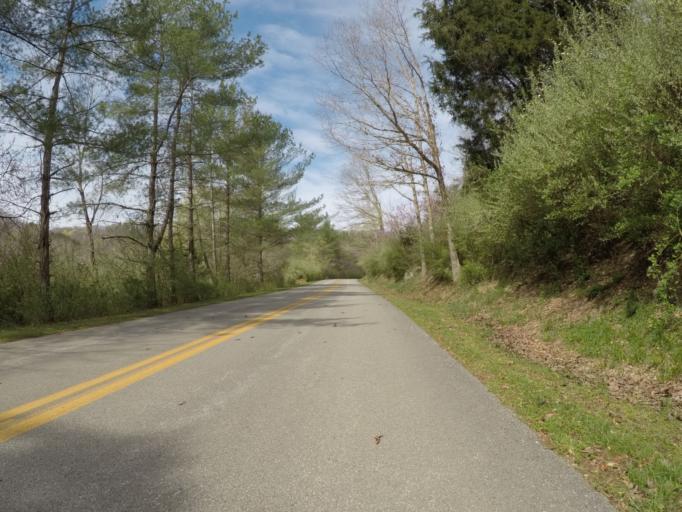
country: US
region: West Virginia
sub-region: Wayne County
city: Lavalette
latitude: 38.3079
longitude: -82.3529
